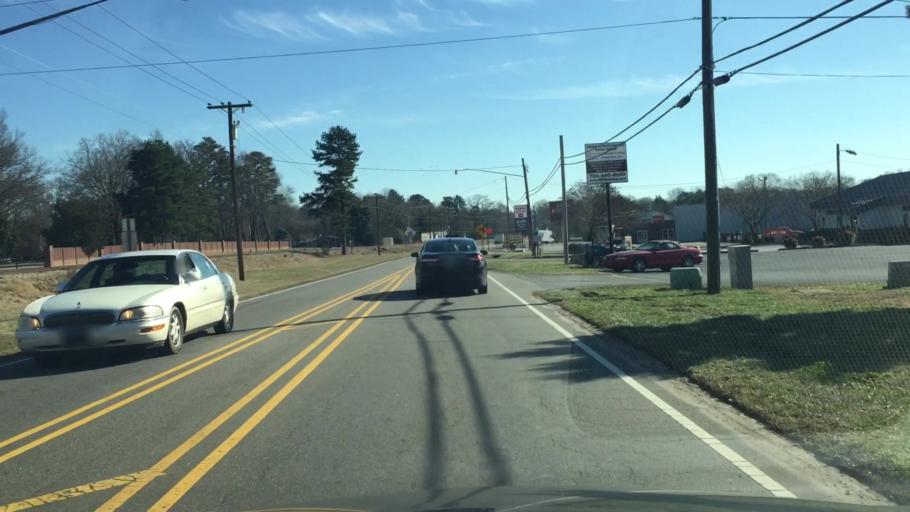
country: US
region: North Carolina
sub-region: Iredell County
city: Mooresville
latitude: 35.5995
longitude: -80.8105
